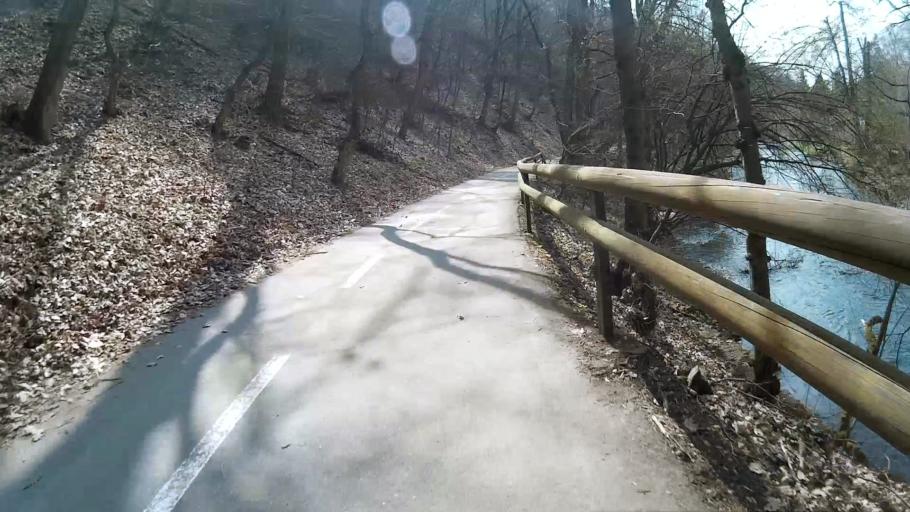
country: CZ
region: South Moravian
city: Bilovice nad Svitavou
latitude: 49.2333
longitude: 16.6734
